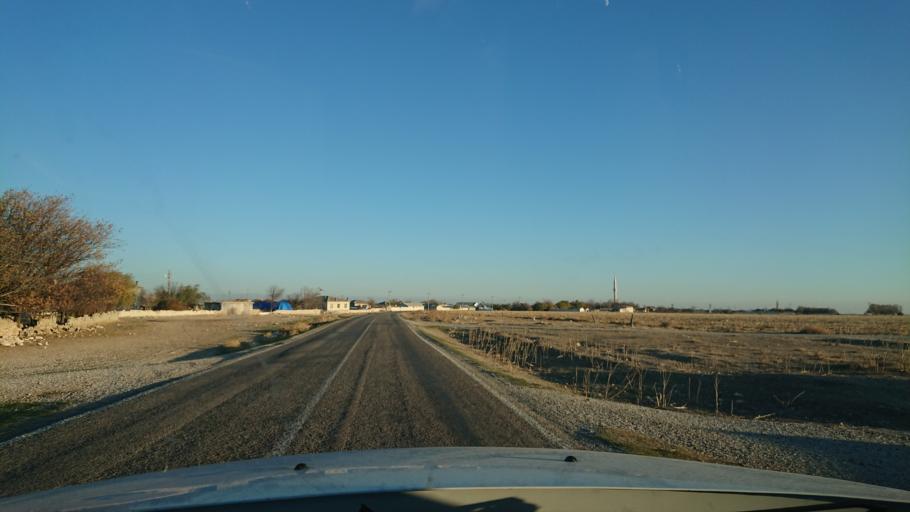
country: TR
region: Aksaray
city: Eskil
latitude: 38.4285
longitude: 33.2780
